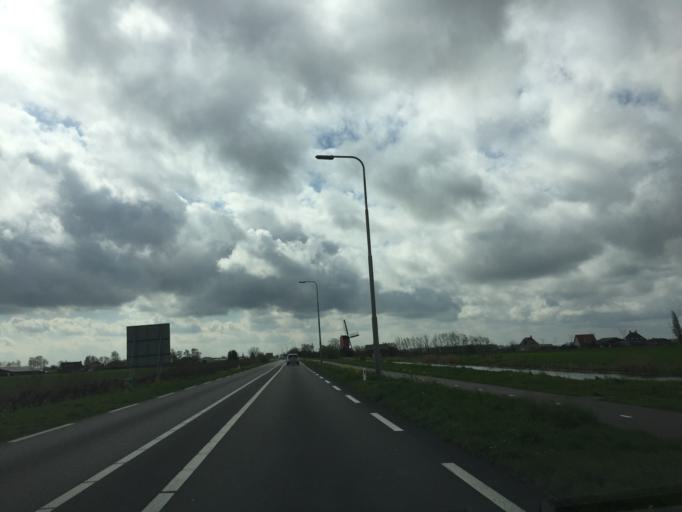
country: NL
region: South Holland
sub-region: Gemeente Rijnwoude
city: Benthuizen
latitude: 52.1192
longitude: 4.5854
